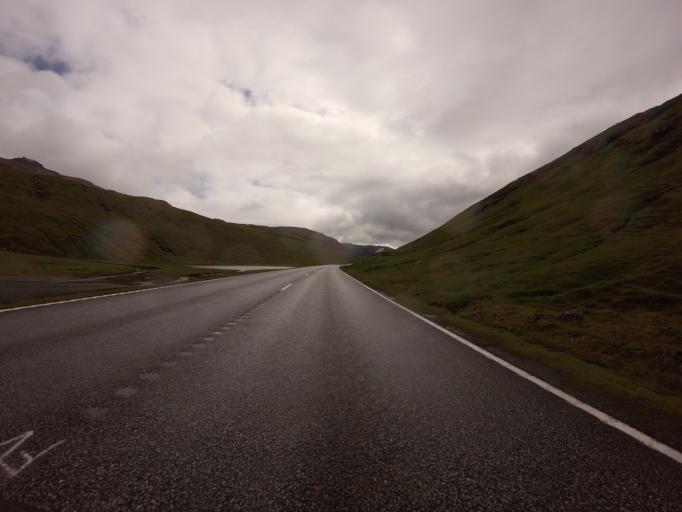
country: FO
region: Streymoy
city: Kollafjordhur
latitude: 62.1263
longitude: -7.0005
